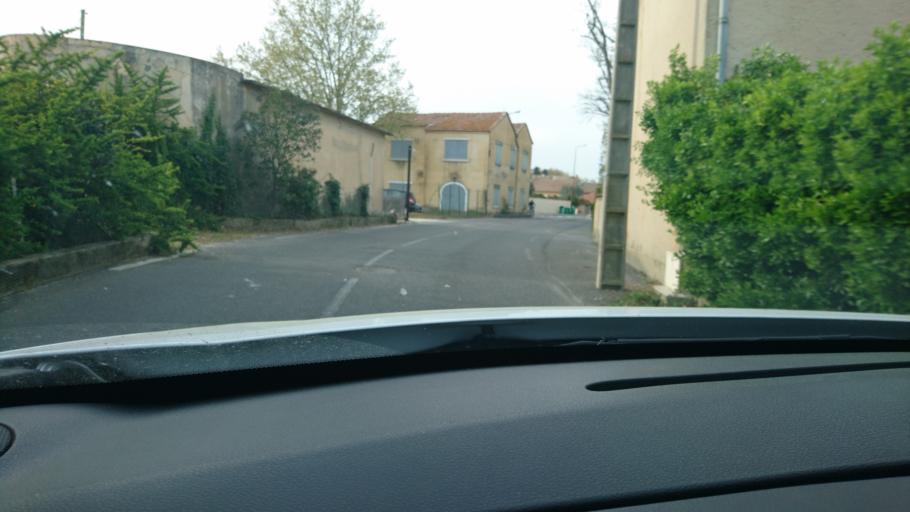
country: FR
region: Provence-Alpes-Cote d'Azur
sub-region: Departement du Vaucluse
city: Montfavet
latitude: 43.9332
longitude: 4.8802
